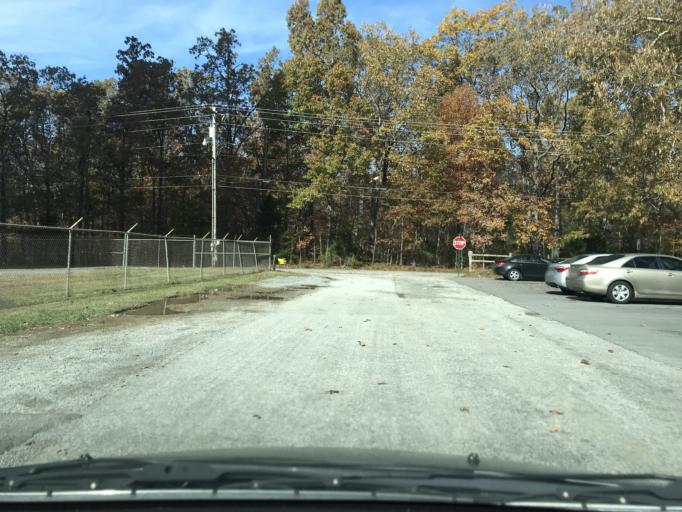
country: US
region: Tennessee
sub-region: Coffee County
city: Tullahoma
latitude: 35.4071
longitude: -86.1745
